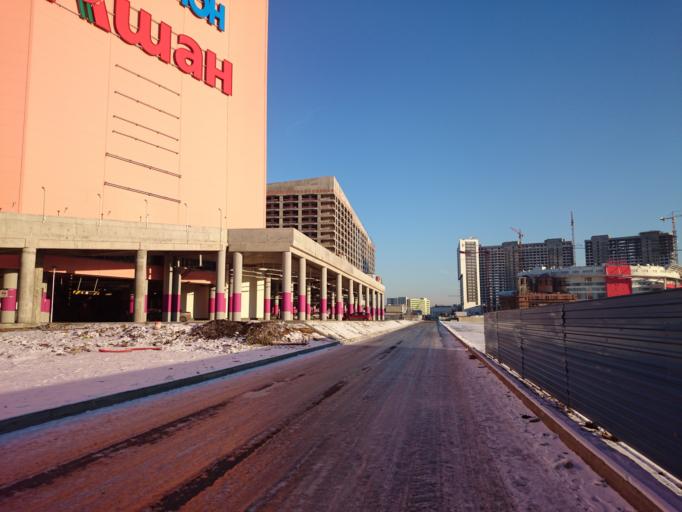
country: RU
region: Moscow
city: Sokol
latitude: 55.7886
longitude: 37.5327
